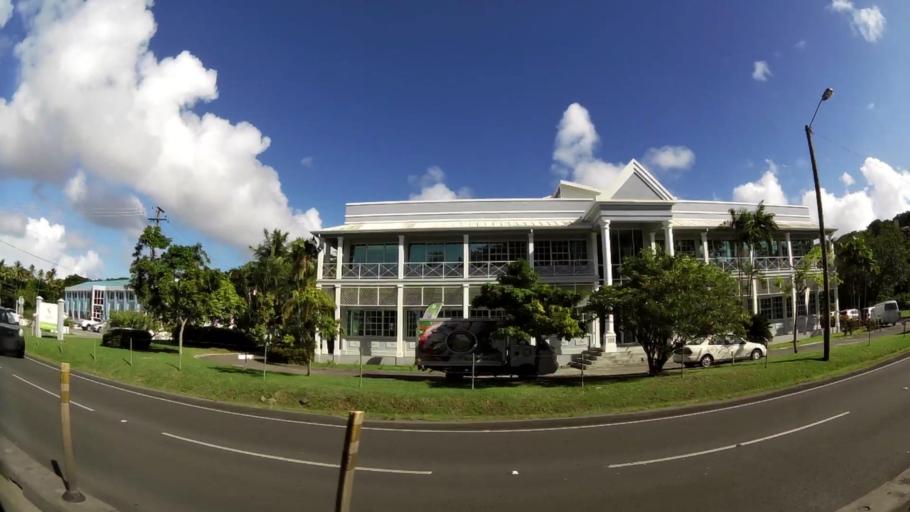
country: LC
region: Castries Quarter
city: Bisee
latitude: 14.0342
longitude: -60.9738
